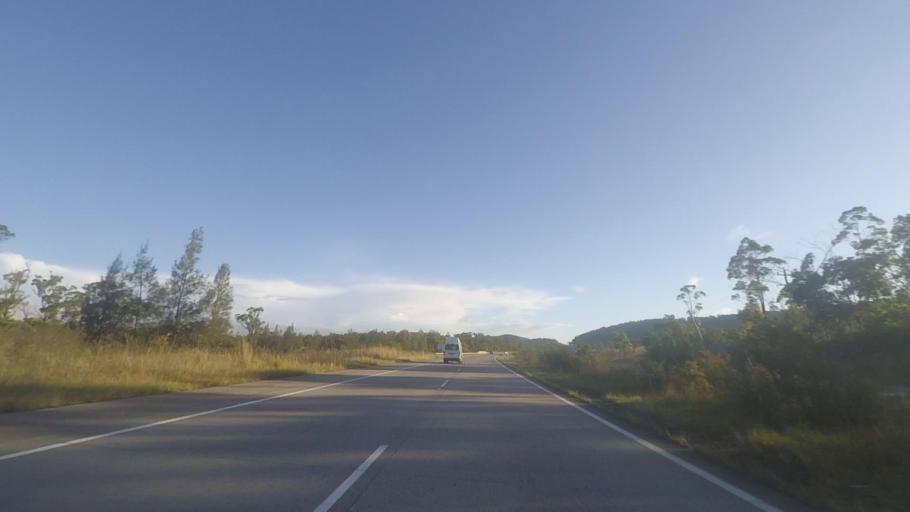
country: AU
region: New South Wales
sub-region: Great Lakes
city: Bulahdelah
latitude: -32.4535
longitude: 152.1979
